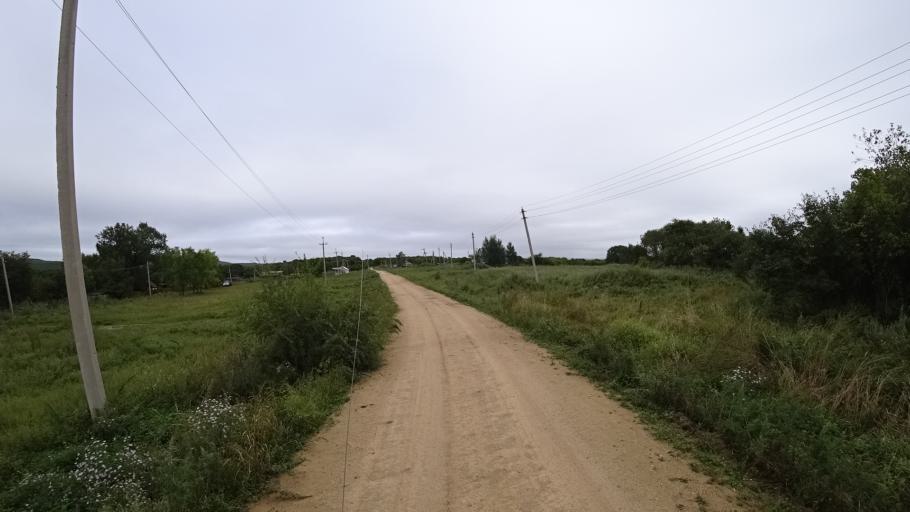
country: RU
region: Primorskiy
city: Rettikhovka
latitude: 44.0566
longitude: 132.6559
